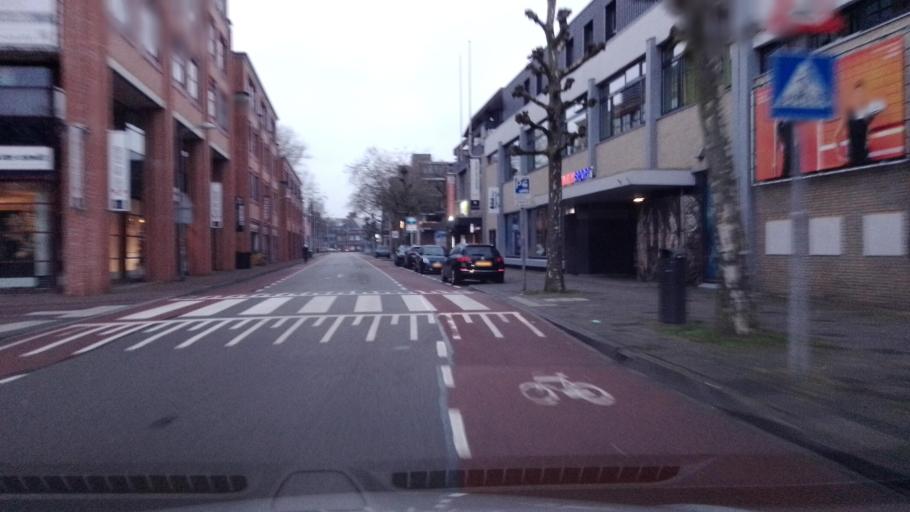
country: NL
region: Gelderland
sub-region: Gemeente Wageningen
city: Wageningen
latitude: 51.9664
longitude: 5.6615
